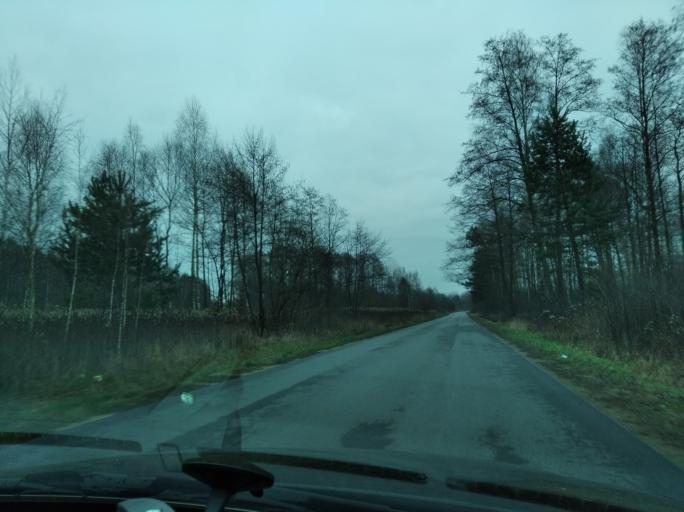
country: PL
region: Subcarpathian Voivodeship
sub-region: Powiat lancucki
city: Rakszawa
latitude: 50.1629
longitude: 22.2140
